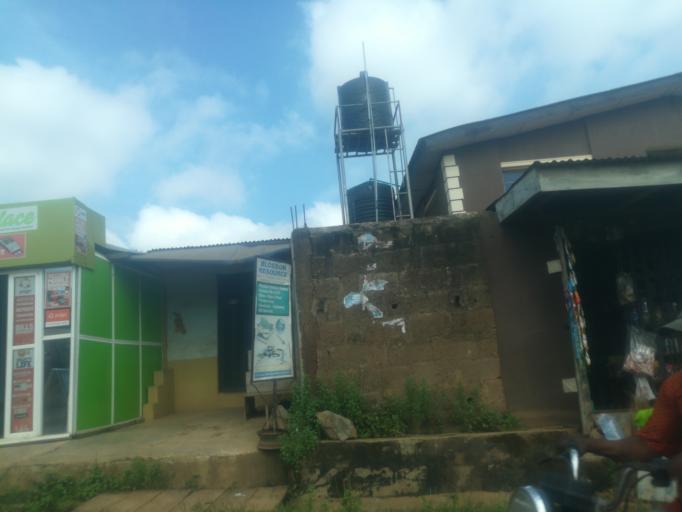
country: NG
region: Oyo
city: Ibadan
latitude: 7.3339
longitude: 3.8535
